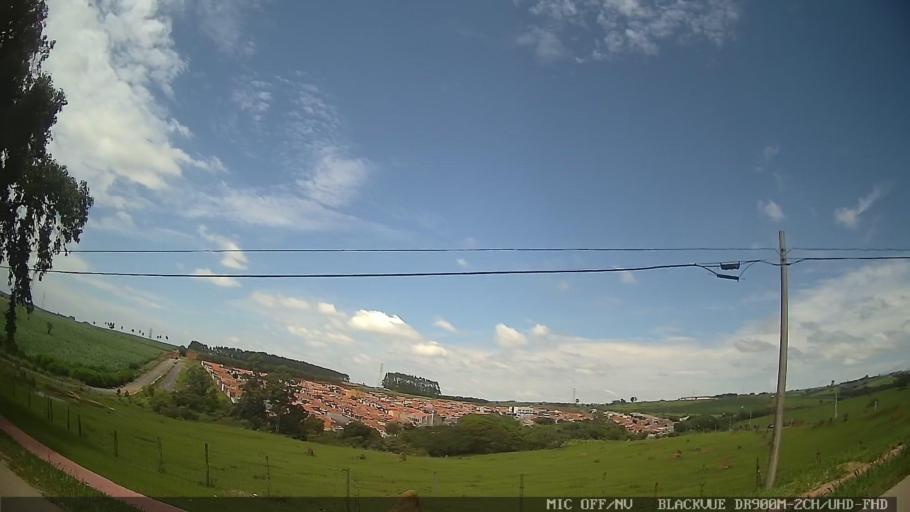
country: BR
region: Sao Paulo
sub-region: Laranjal Paulista
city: Laranjal Paulista
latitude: -23.0658
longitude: -47.8274
